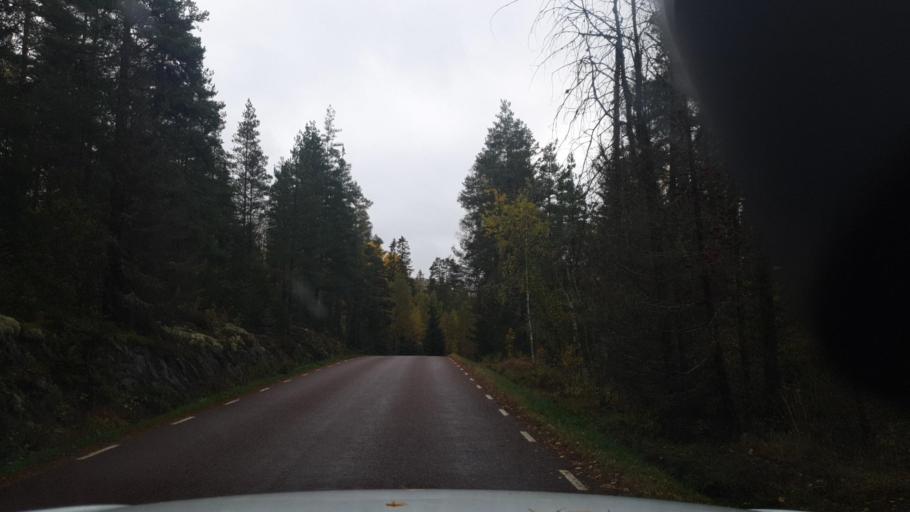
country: SE
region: Vaermland
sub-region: Grums Kommun
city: Grums
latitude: 59.4211
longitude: 13.0868
